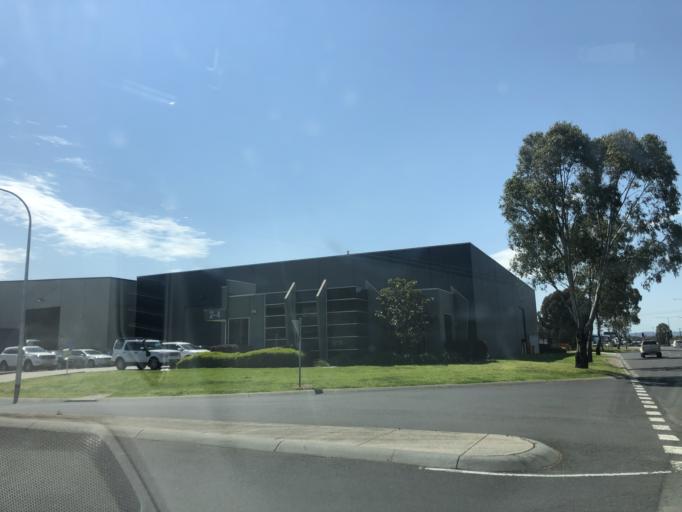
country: AU
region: Victoria
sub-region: Casey
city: Hampton Park
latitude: -38.0223
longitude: 145.2375
